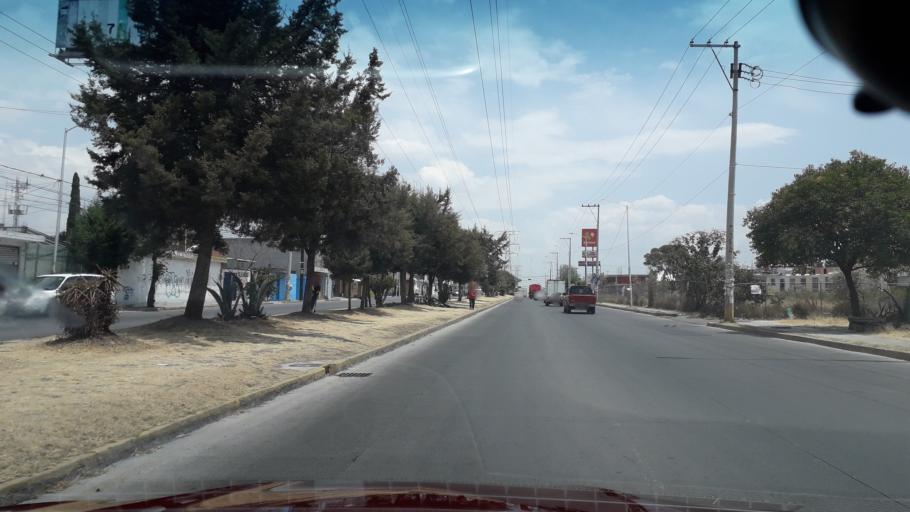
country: MX
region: Puebla
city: Puebla
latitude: 19.0027
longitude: -98.2327
